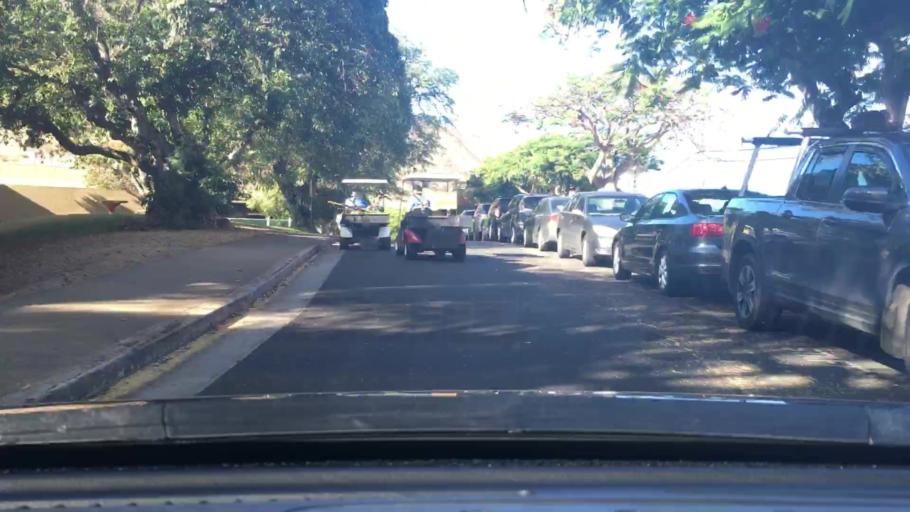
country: US
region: Hawaii
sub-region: Honolulu County
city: Honolulu
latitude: 21.2718
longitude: -157.8019
